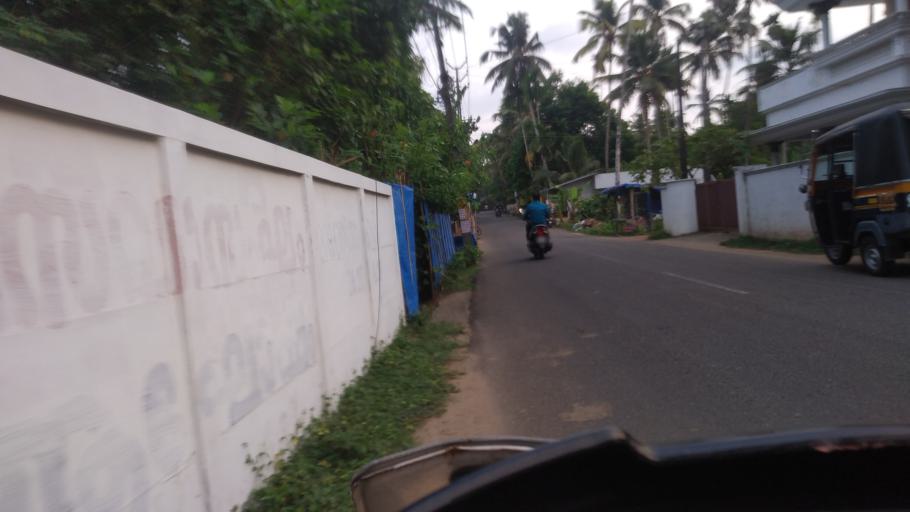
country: IN
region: Kerala
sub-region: Thrissur District
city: Kodungallur
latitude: 10.1693
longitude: 76.1984
